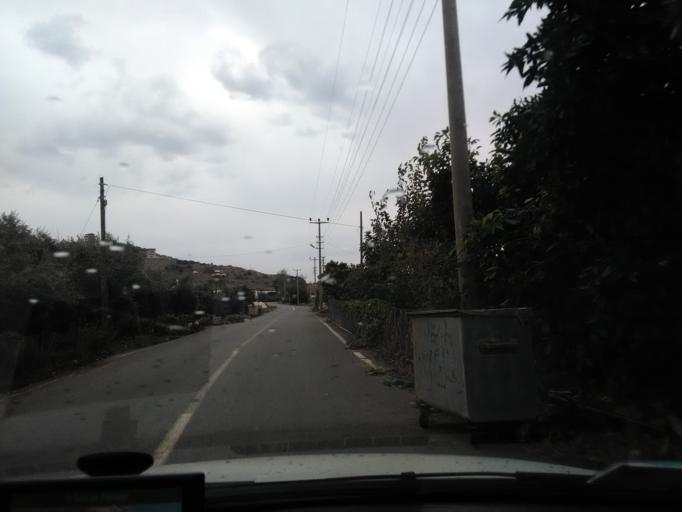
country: TR
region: Antalya
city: Gazipasa
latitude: 36.2470
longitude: 32.3027
